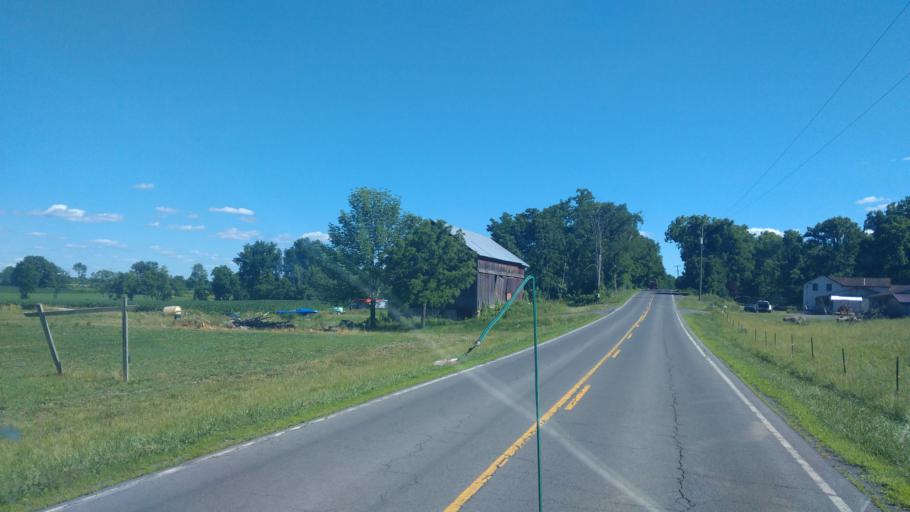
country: US
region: New York
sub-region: Seneca County
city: Seneca Falls
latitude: 42.9851
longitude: -76.8003
